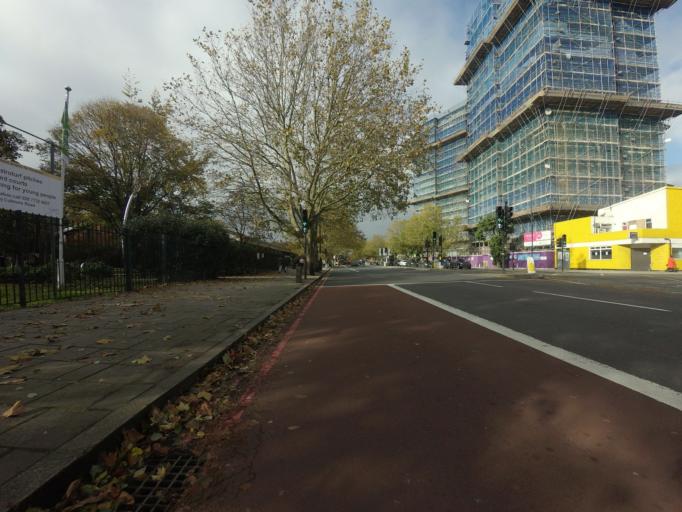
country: GB
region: England
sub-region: Greater London
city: Camberwell
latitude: 51.4786
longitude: -0.0548
